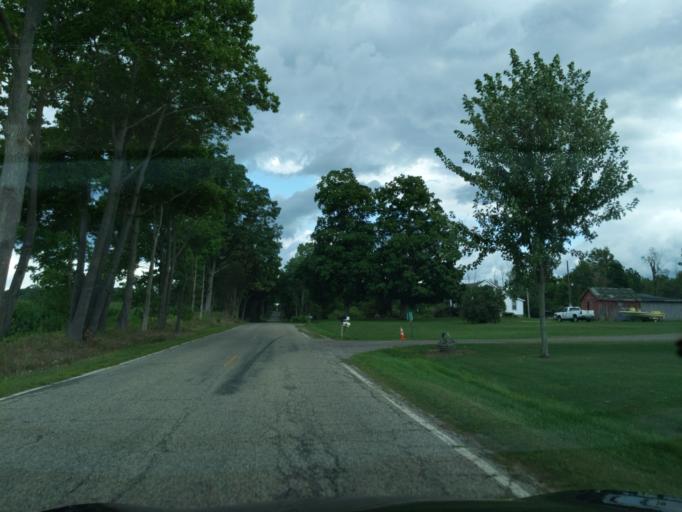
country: US
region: Michigan
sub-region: Ingham County
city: Leslie
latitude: 42.3787
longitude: -84.5629
